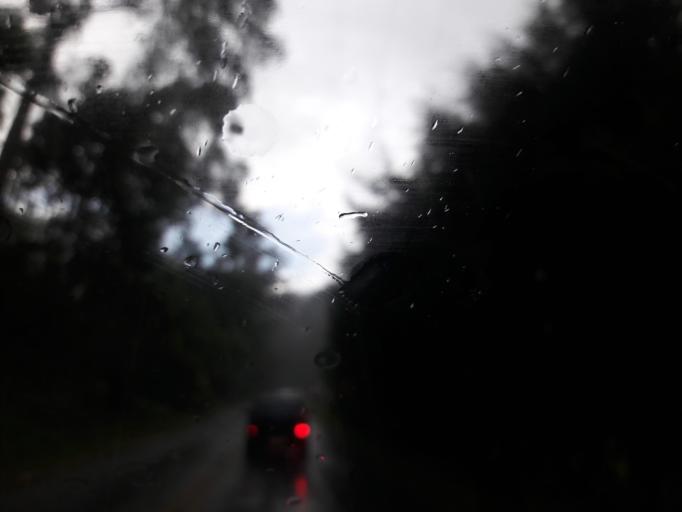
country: BR
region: Sao Paulo
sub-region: Bom Jesus Dos Perdoes
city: Bom Jesus dos Perdoes
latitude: -23.2603
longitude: -46.4180
